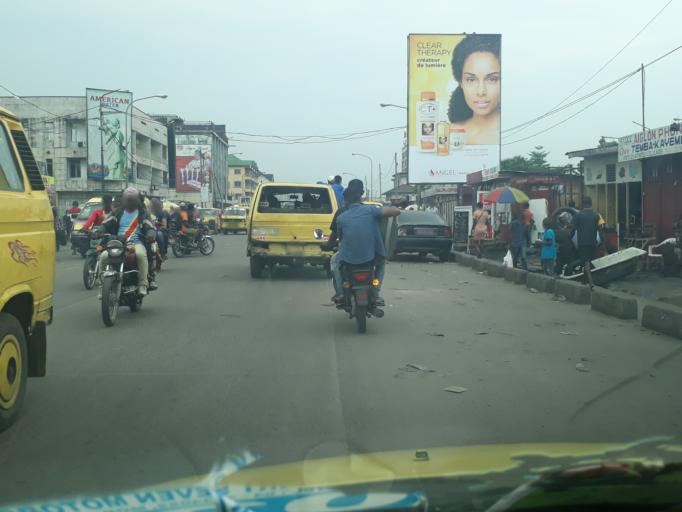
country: CD
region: Kinshasa
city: Kinshasa
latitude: -4.3441
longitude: 15.3127
